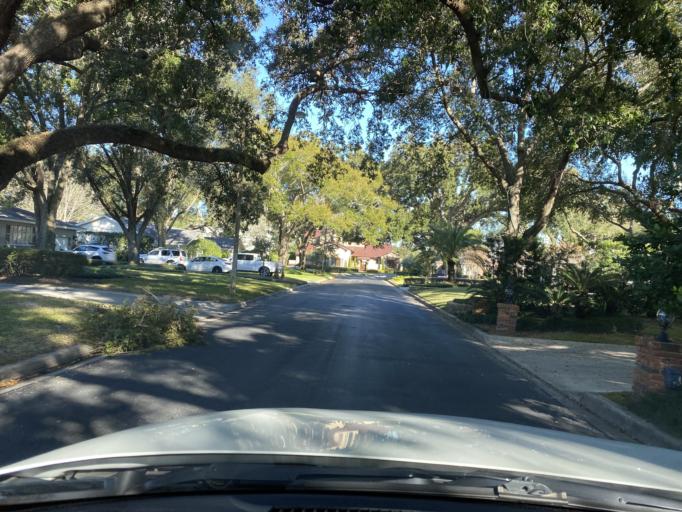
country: US
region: Florida
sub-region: Orange County
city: Orlando
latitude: 28.5552
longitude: -81.4045
